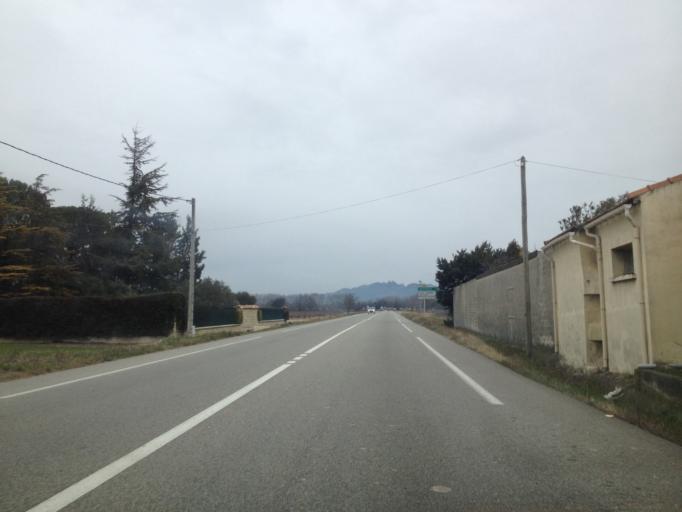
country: FR
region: Provence-Alpes-Cote d'Azur
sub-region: Departement du Vaucluse
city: Jonquieres
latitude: 44.1001
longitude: 4.9057
